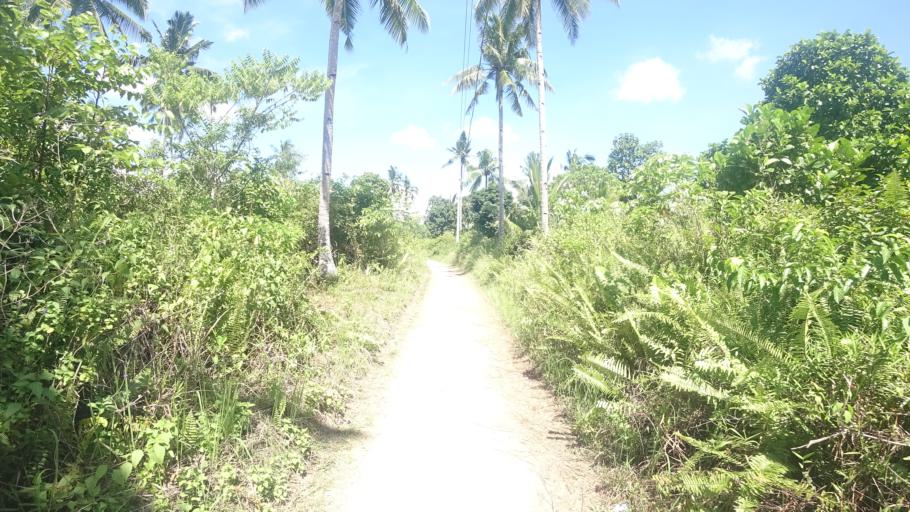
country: PH
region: Eastern Visayas
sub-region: Province of Leyte
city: Liberty
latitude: 10.8867
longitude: 125.0076
